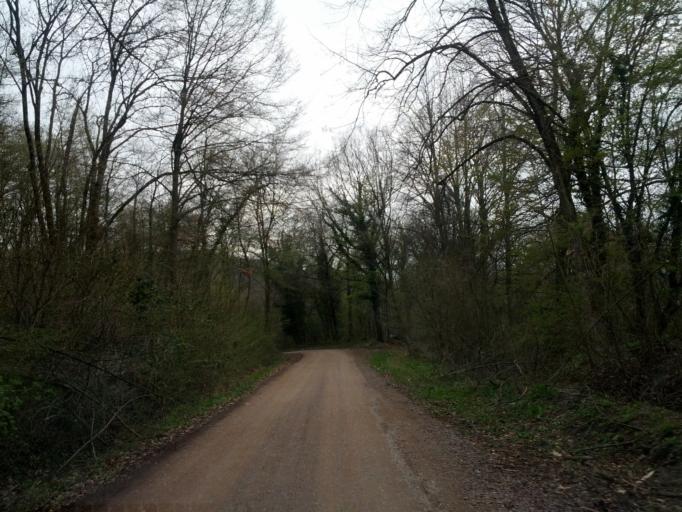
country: DE
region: Baden-Wuerttemberg
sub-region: Freiburg Region
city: Ebringen
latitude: 47.9573
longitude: 7.7931
